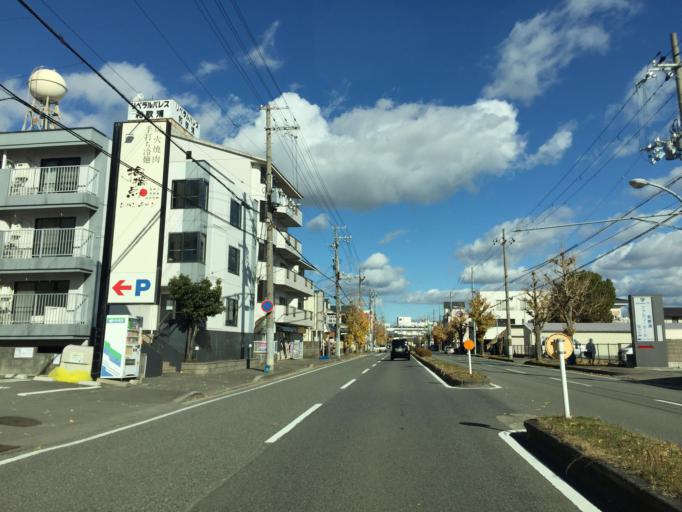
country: JP
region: Wakayama
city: Minato
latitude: 34.1914
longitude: 135.1759
